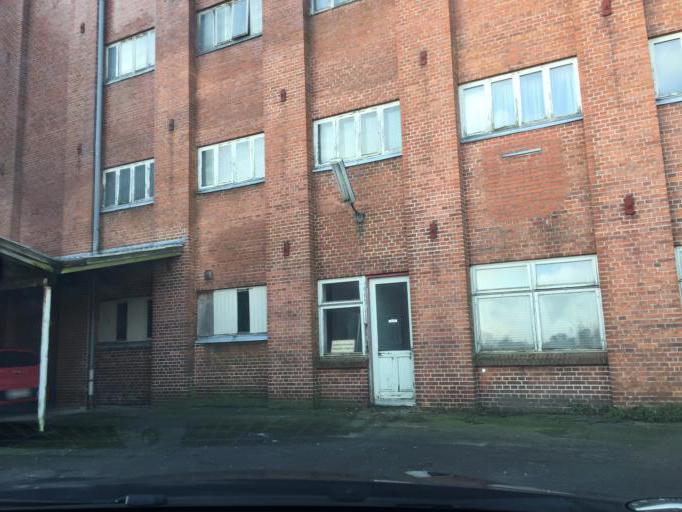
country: DK
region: South Denmark
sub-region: Faaborg-Midtfyn Kommune
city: Ringe
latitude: 55.1918
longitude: 10.3487
